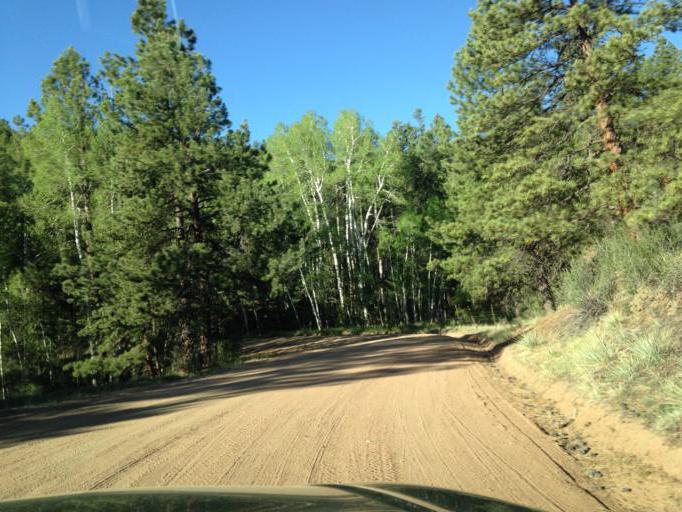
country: US
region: Colorado
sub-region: Jefferson County
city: Evergreen
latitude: 39.4106
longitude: -105.5271
